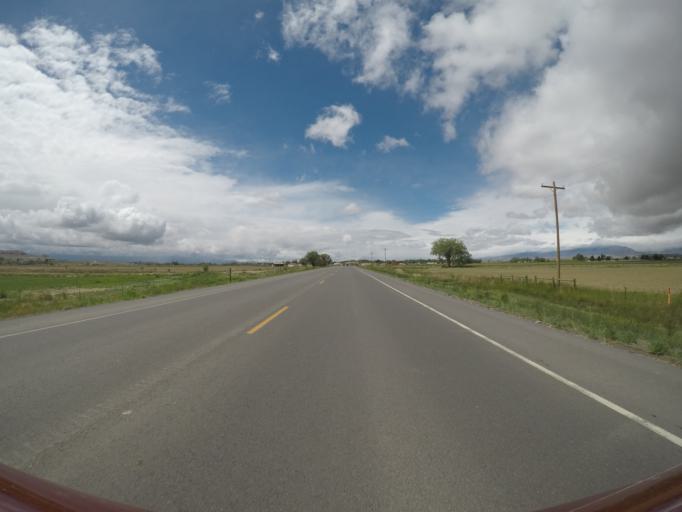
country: US
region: Wyoming
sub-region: Big Horn County
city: Lovell
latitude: 44.8686
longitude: -108.4543
